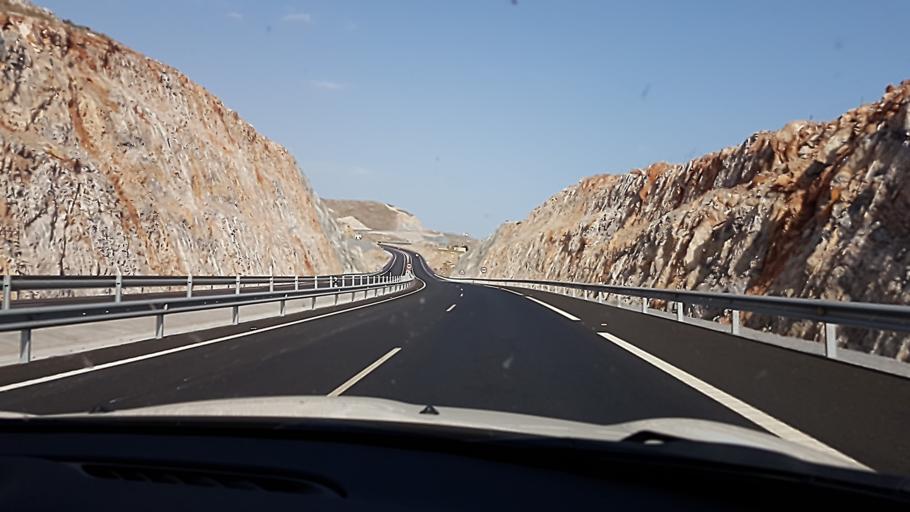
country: ES
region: Andalusia
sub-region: Provincia de Granada
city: Gualchos
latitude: 36.7098
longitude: -3.4091
